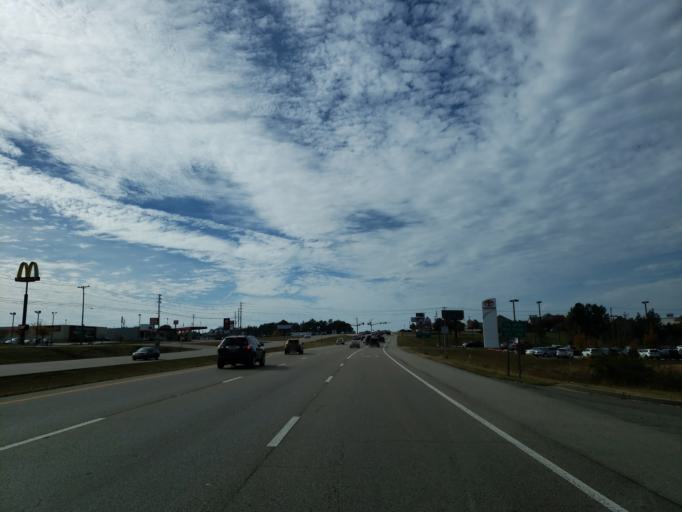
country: US
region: Mississippi
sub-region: Lamar County
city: West Hattiesburg
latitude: 31.3177
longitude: -89.4091
